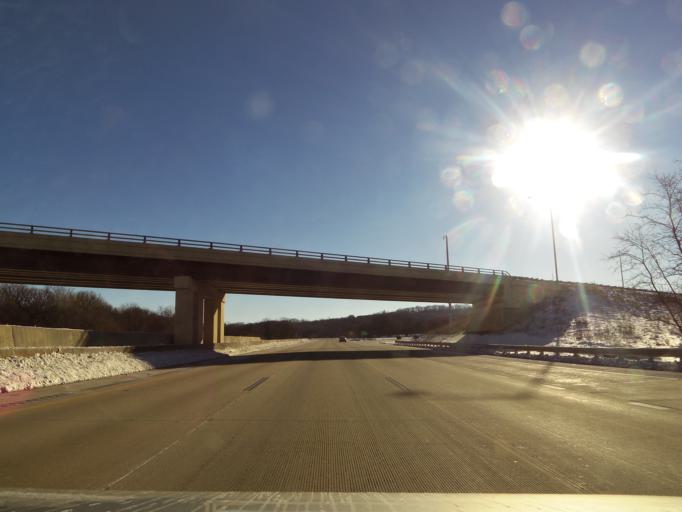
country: US
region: Wisconsin
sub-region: Columbia County
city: Poynette
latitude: 43.3925
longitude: -89.4670
